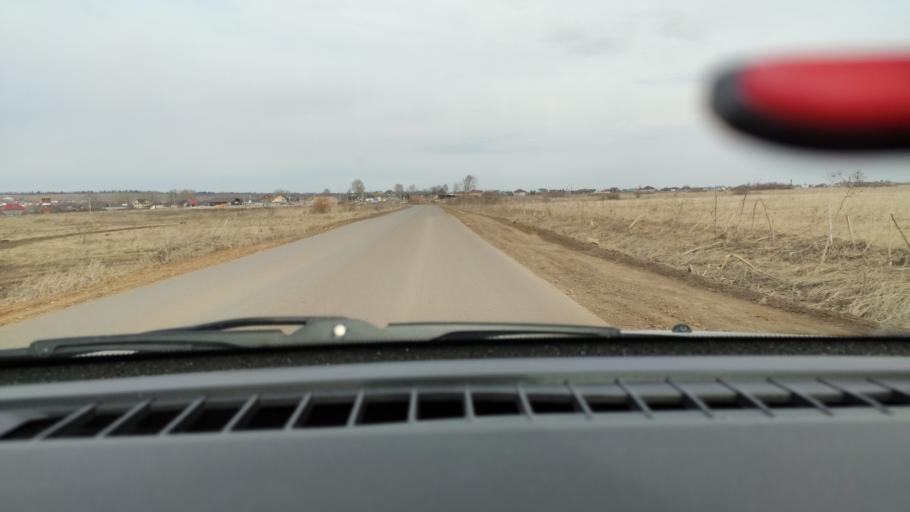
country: RU
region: Perm
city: Kultayevo
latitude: 57.9032
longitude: 55.9923
